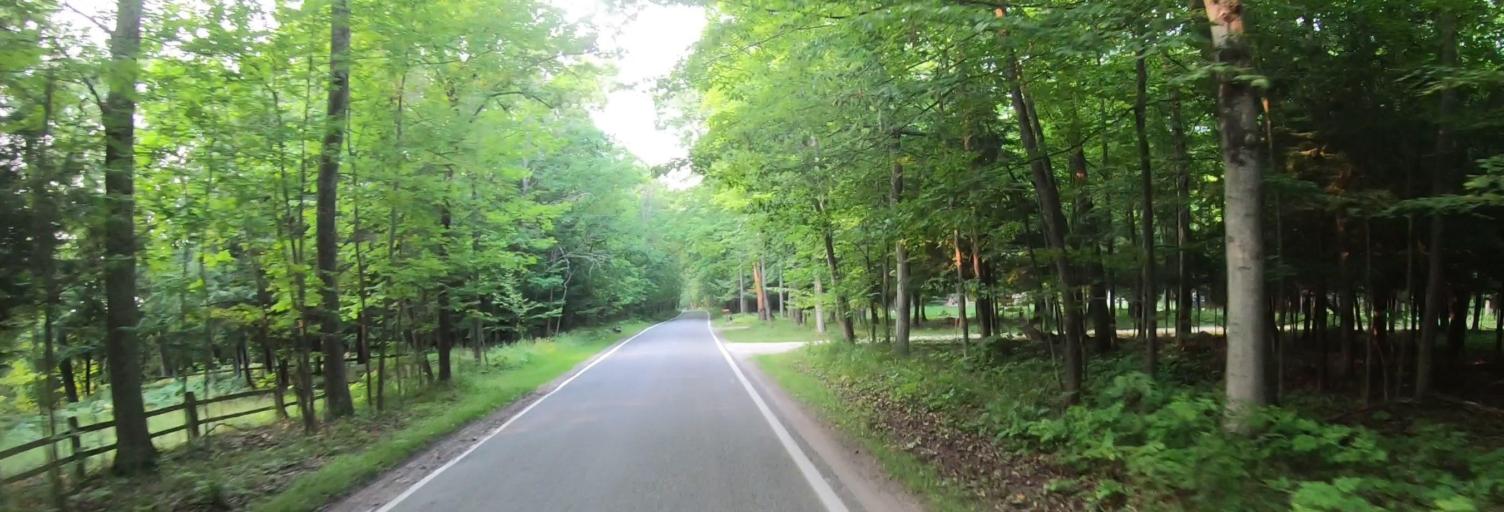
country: US
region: Michigan
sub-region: Emmet County
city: Harbor Springs
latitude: 45.5760
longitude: -85.1130
